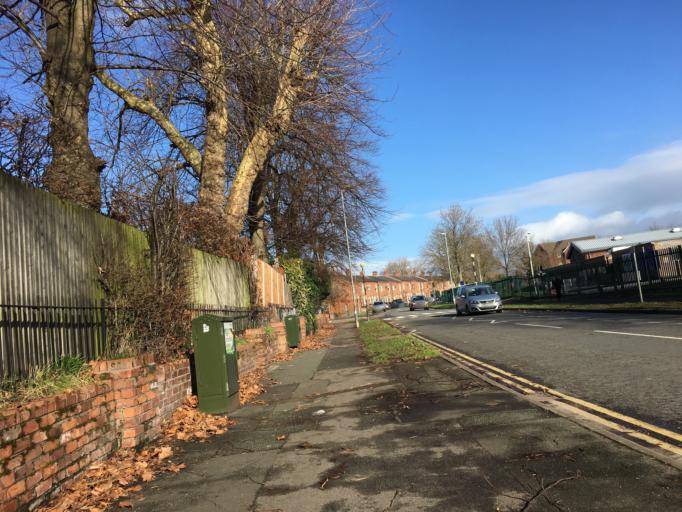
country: GB
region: England
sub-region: Cheshire West and Chester
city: Hoole
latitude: 53.1972
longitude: -2.8679
